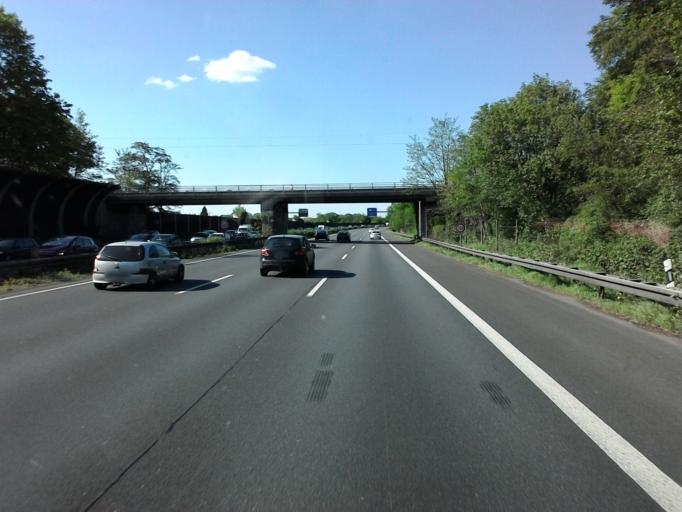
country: DE
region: North Rhine-Westphalia
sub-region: Regierungsbezirk Dusseldorf
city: Duisburg
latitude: 51.4152
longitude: 6.7984
